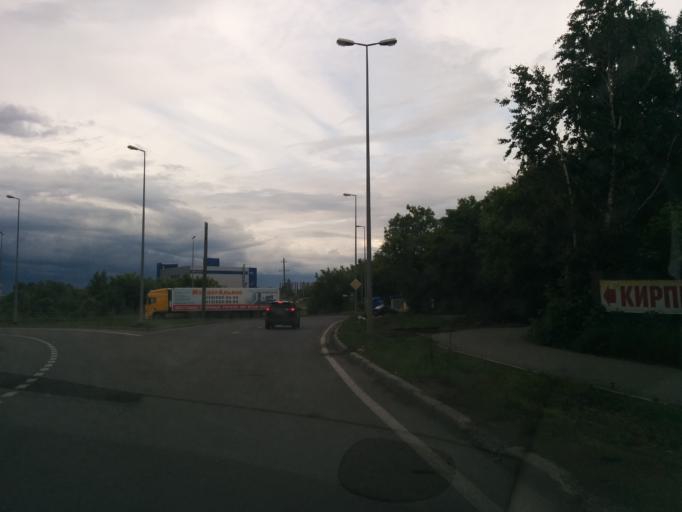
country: RU
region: Perm
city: Kondratovo
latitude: 57.9999
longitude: 56.1339
